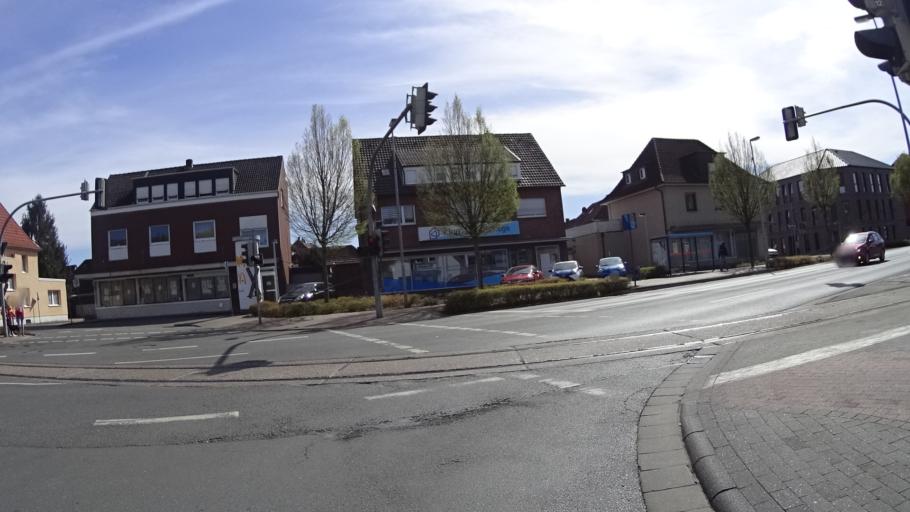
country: DE
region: North Rhine-Westphalia
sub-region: Regierungsbezirk Munster
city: Dreierwalde
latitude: 52.2864
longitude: 7.4748
